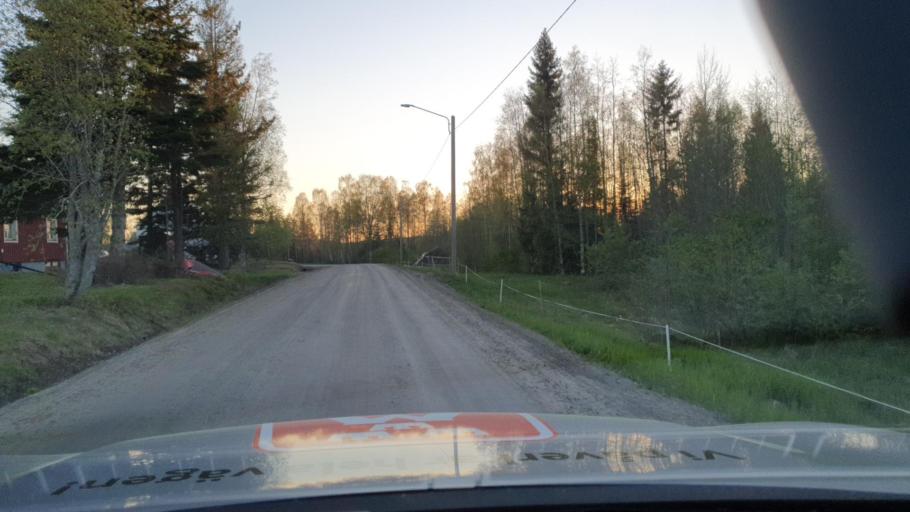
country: SE
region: Vaesternorrland
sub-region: OErnskoeldsviks Kommun
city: Bjasta
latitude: 63.5067
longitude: 18.4726
